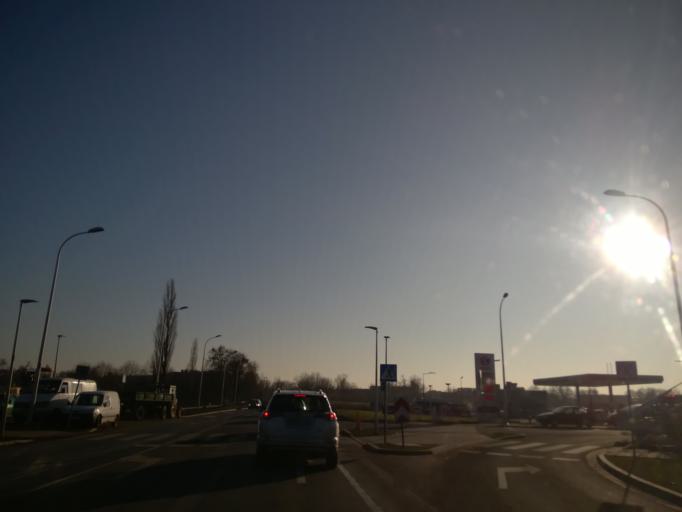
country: PL
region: Lower Silesian Voivodeship
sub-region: Powiat wroclawski
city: Bielany Wroclawskie
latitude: 51.0821
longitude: 16.9559
